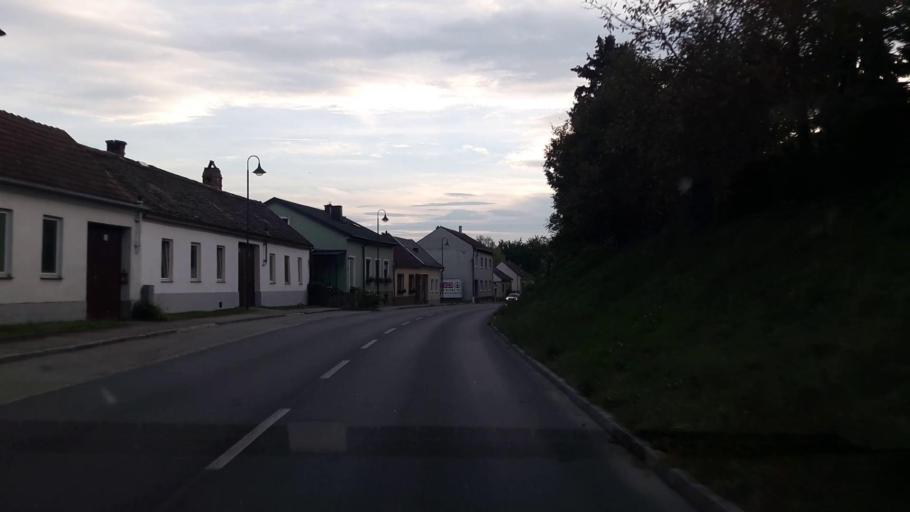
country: AT
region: Lower Austria
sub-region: Politischer Bezirk Korneuburg
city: Harmannsdorf
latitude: 48.3847
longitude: 16.3597
